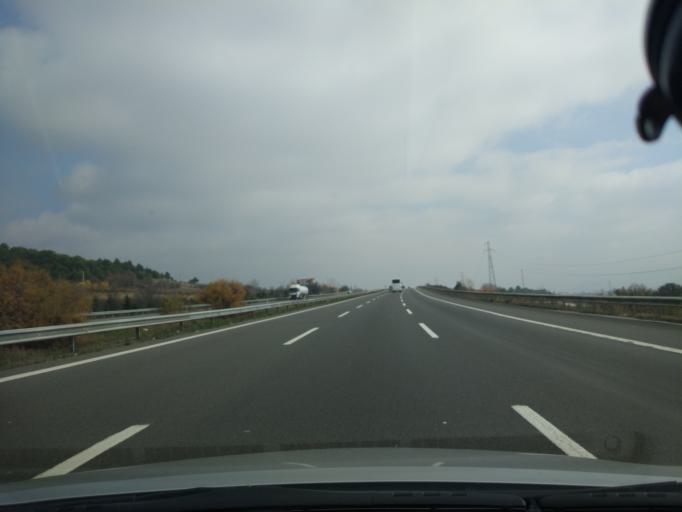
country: TR
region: Bolu
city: Bolu
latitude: 40.7628
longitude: 31.6056
